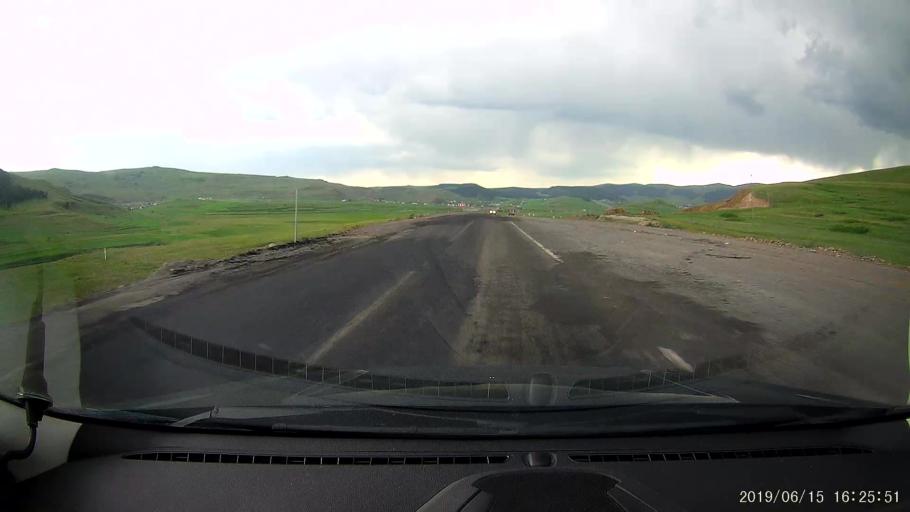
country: TR
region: Ardahan
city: Hanak
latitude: 41.1485
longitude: 42.8662
